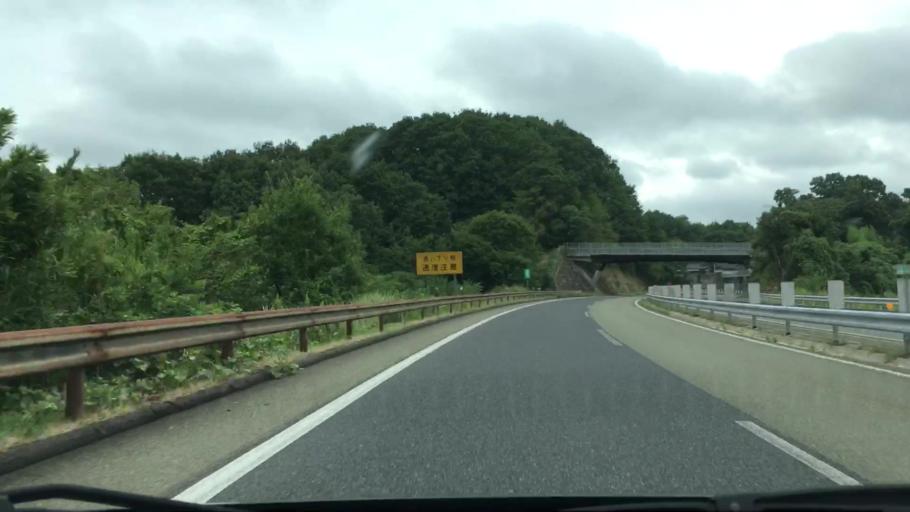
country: JP
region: Hiroshima
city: Shobara
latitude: 34.8282
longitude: 133.0505
